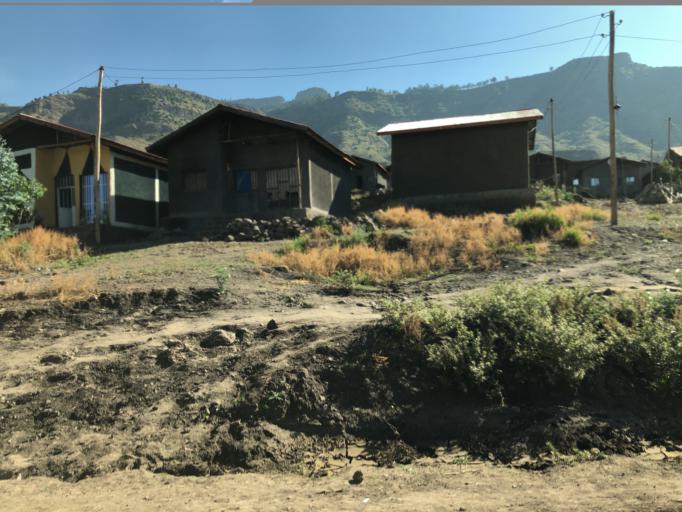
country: ET
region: Amhara
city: Lalibela
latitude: 12.0137
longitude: 39.0527
